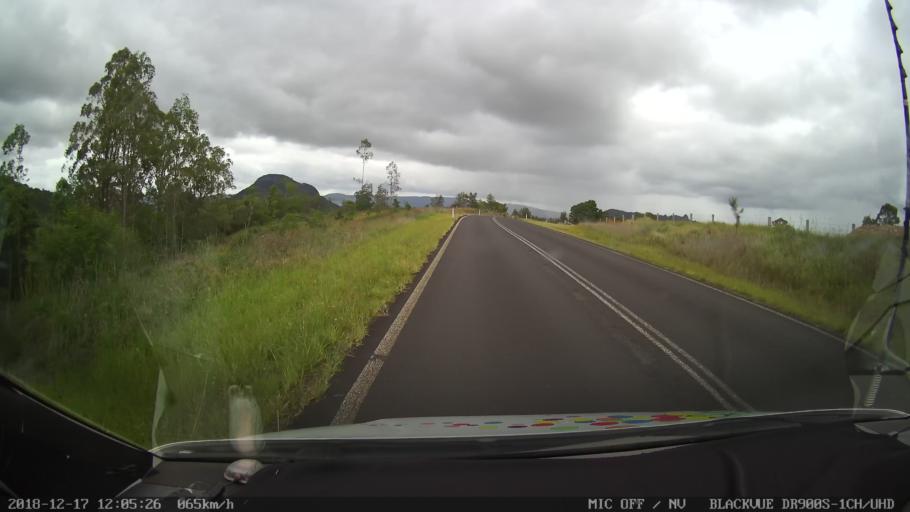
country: AU
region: New South Wales
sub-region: Kyogle
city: Kyogle
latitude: -28.4926
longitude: 152.5668
